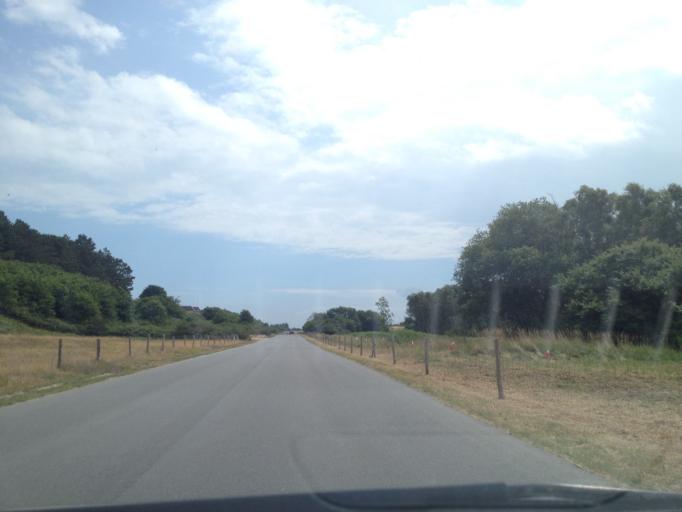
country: DK
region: Central Jutland
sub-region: Syddjurs Kommune
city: Ebeltoft
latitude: 56.1554
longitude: 10.6806
